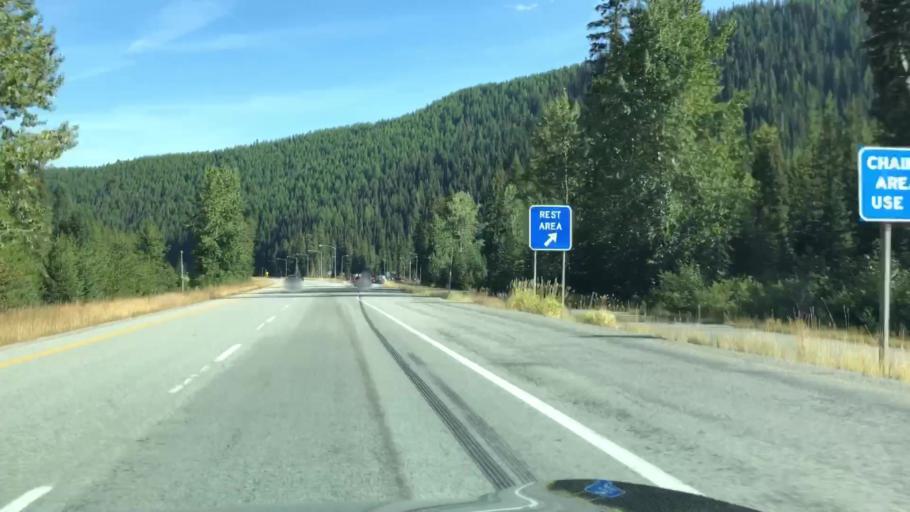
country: US
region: Idaho
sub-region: Shoshone County
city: Wallace
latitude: 47.4219
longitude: -115.6332
